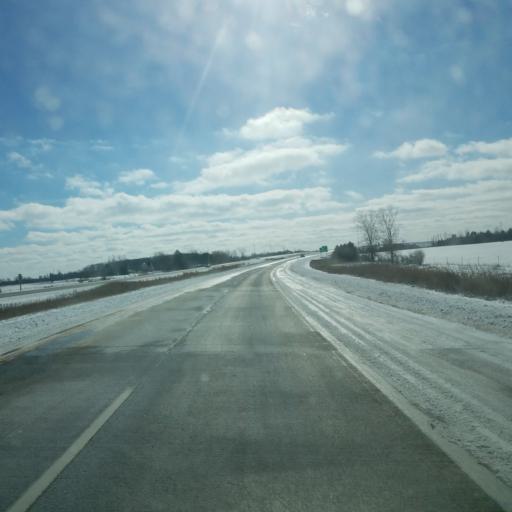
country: US
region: Michigan
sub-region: Clinton County
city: Saint Johns
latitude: 43.0126
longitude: -84.5197
